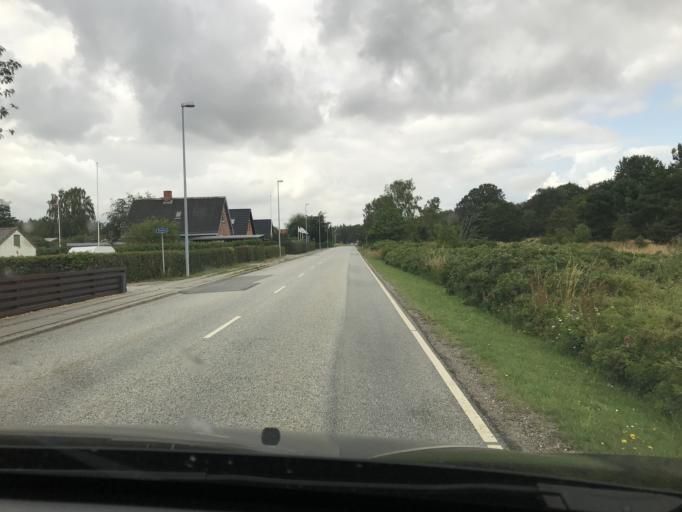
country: DK
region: Central Jutland
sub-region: Norddjurs Kommune
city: Auning
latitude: 56.3980
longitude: 10.4094
